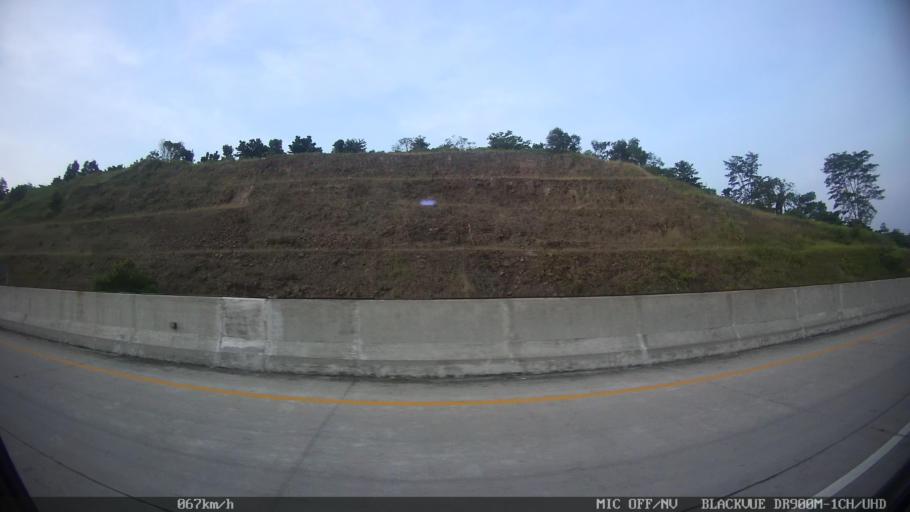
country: ID
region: Lampung
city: Penengahan
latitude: -5.8624
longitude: 105.7395
